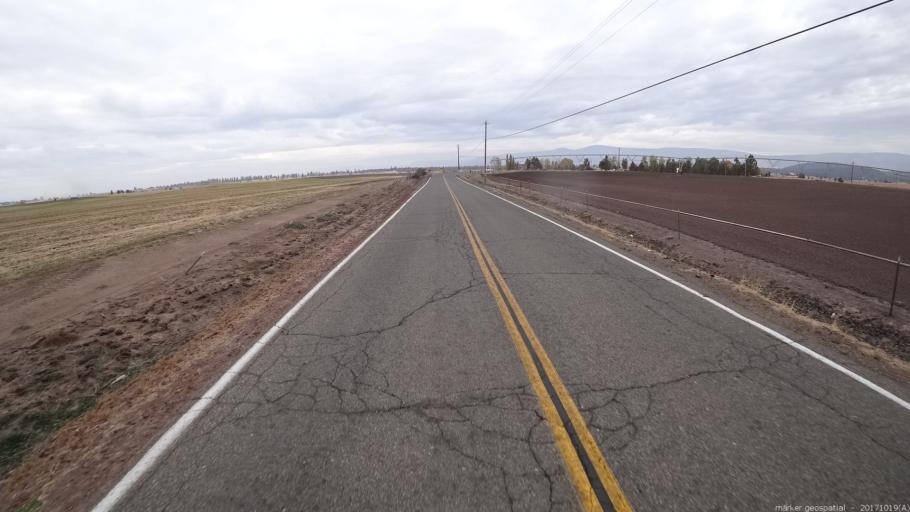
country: US
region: California
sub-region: Shasta County
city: Burney
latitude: 41.0358
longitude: -121.3651
